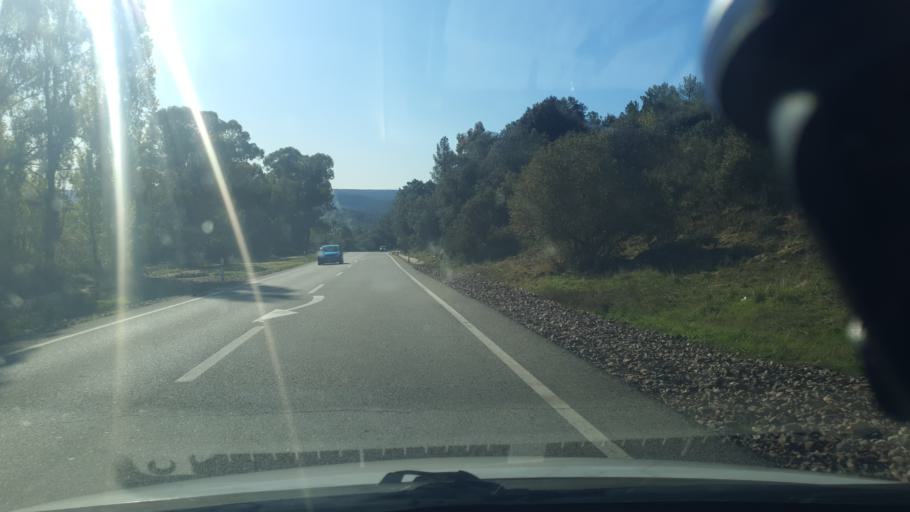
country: ES
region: Castille and Leon
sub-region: Provincia de Avila
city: Arenas de San Pedro
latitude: 40.1919
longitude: -5.0467
